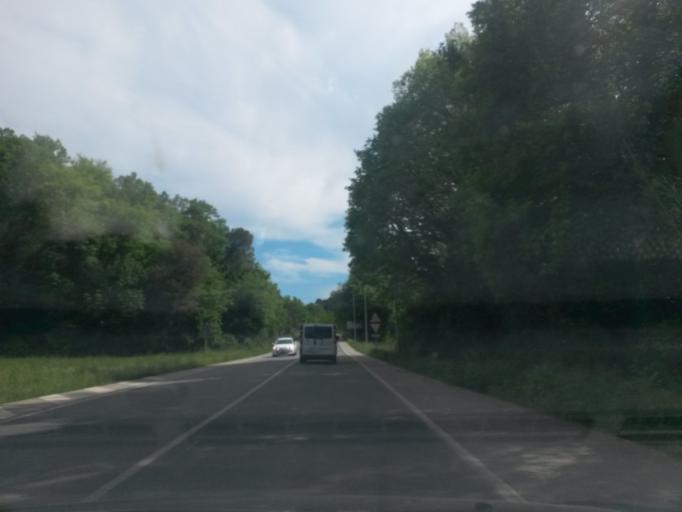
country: ES
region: Catalonia
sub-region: Provincia de Girona
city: Angles
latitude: 41.9521
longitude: 2.6405
